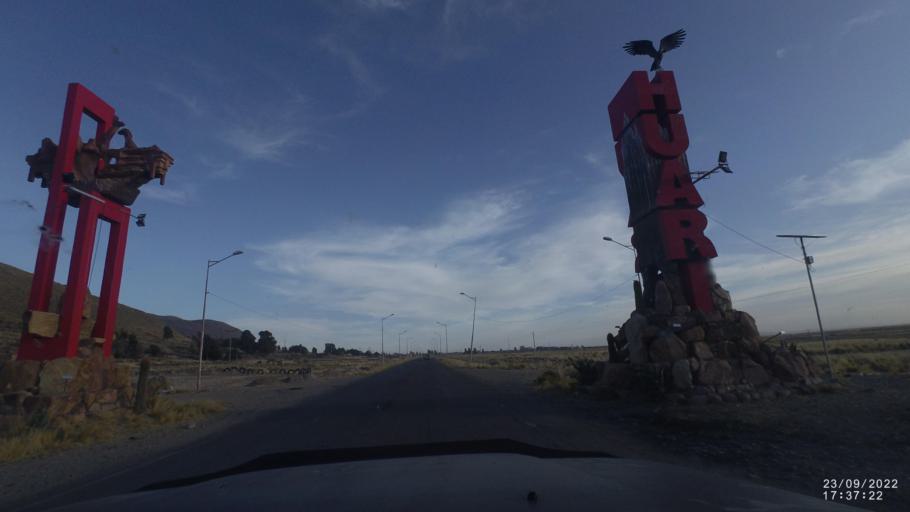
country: BO
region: Oruro
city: Challapata
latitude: -18.9946
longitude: -66.7779
